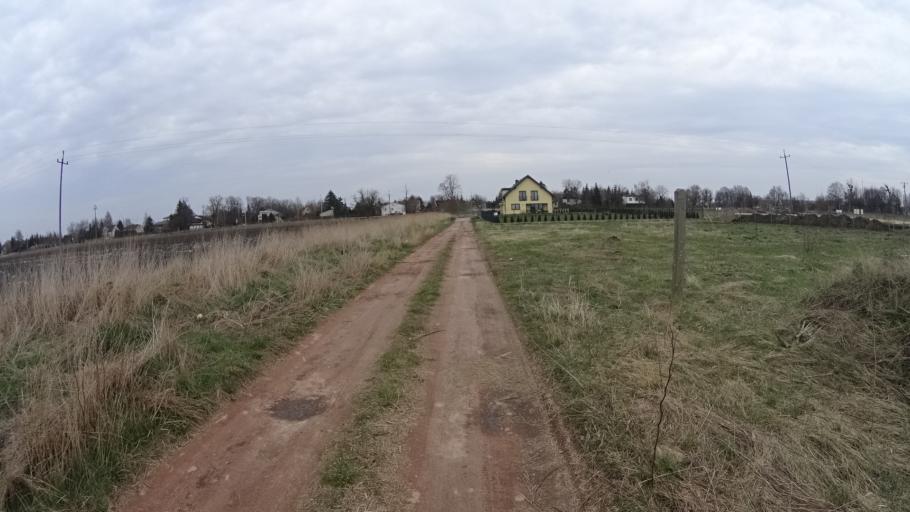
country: PL
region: Masovian Voivodeship
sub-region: Powiat warszawski zachodni
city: Jozefow
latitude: 52.2009
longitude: 20.6944
